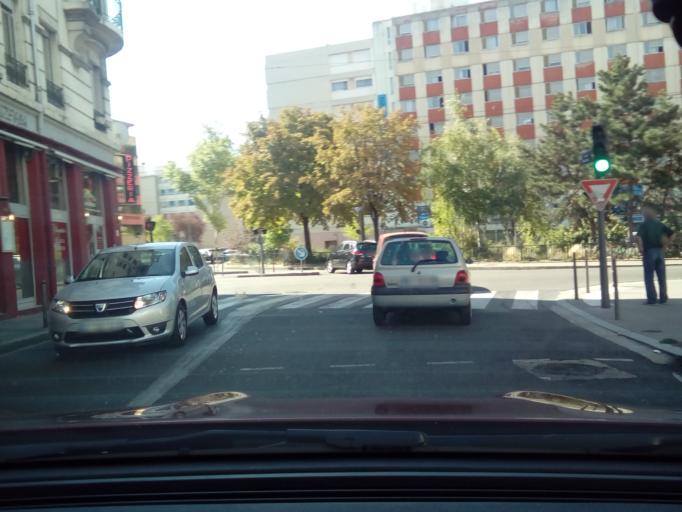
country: FR
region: Rhone-Alpes
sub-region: Departement du Rhone
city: Villeurbanne
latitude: 45.7629
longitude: 4.8781
